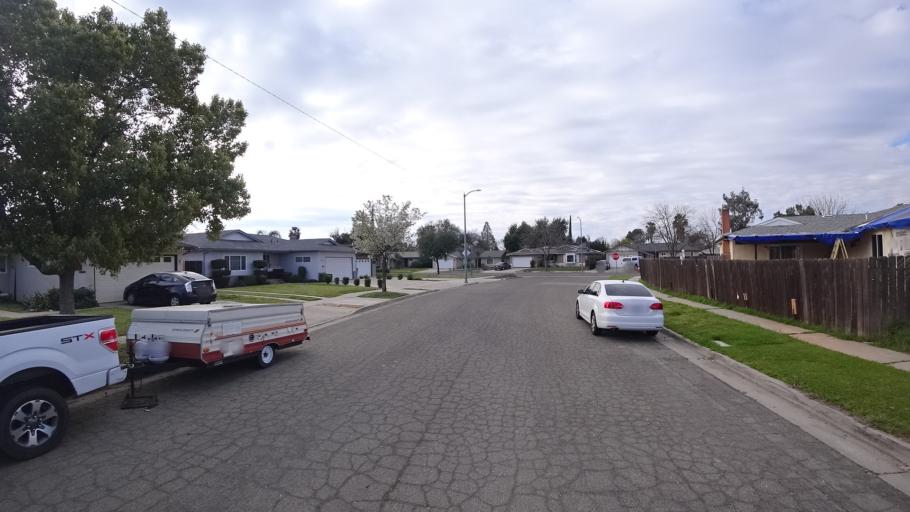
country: US
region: California
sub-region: Fresno County
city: Clovis
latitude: 36.8350
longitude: -119.7582
